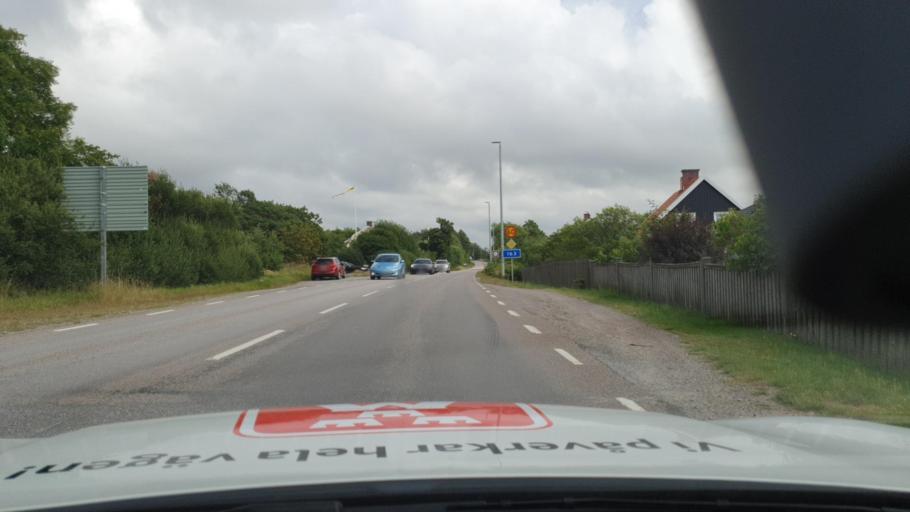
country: SE
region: Vaestra Goetaland
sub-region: Tanums Kommun
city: Grebbestad
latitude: 58.5988
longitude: 11.2932
